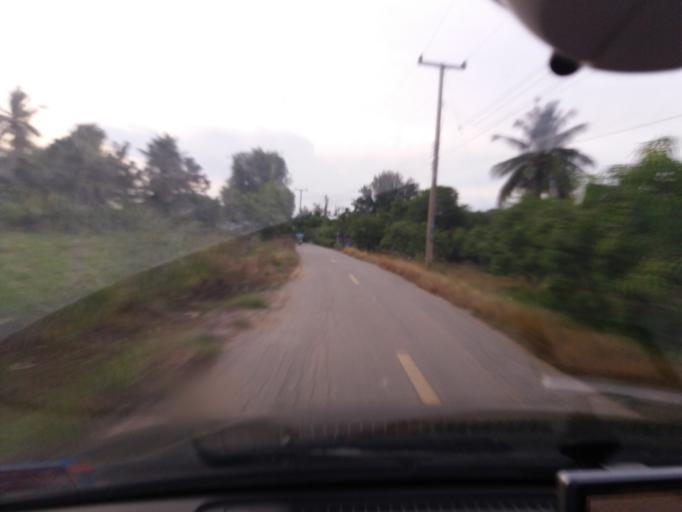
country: TH
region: Suphan Buri
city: Doembang Nangbuat
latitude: 14.8142
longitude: 100.1389
